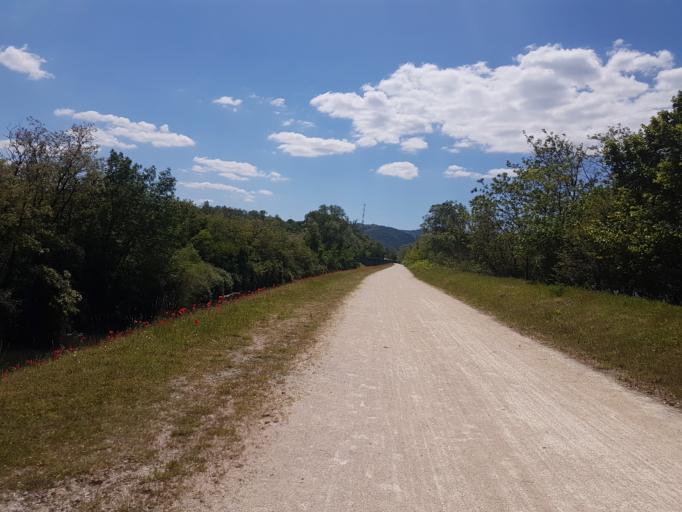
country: FR
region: Rhone-Alpes
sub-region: Departement de l'Ardeche
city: Mauves
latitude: 45.0455
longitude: 4.8550
